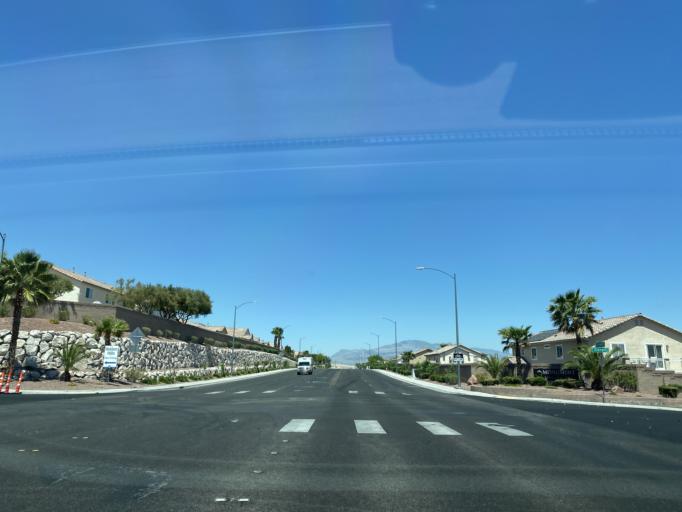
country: US
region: Nevada
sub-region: Clark County
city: Summerlin South
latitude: 36.2418
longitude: -115.3279
